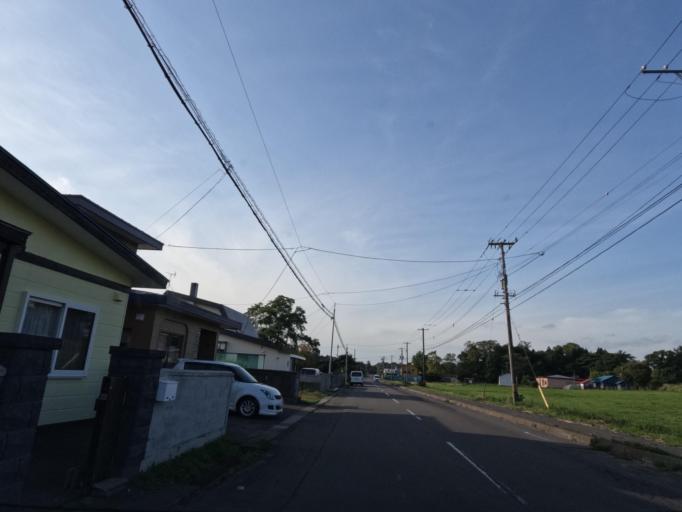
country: JP
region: Hokkaido
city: Date
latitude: 42.4205
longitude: 140.9116
